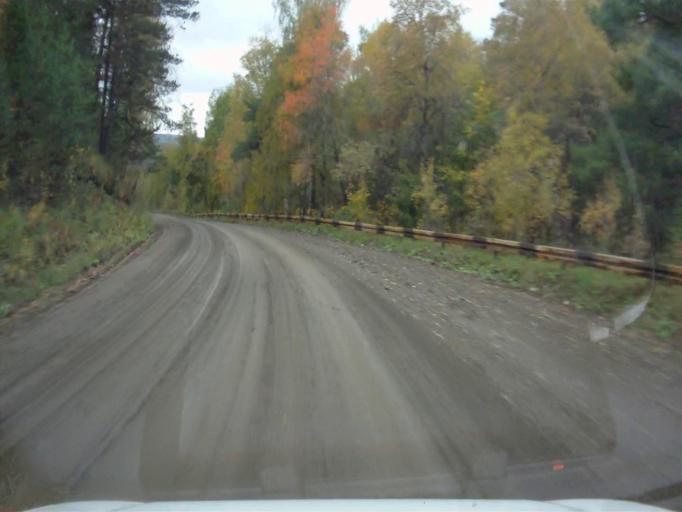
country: RU
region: Chelyabinsk
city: Nyazepetrovsk
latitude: 56.1213
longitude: 59.3679
